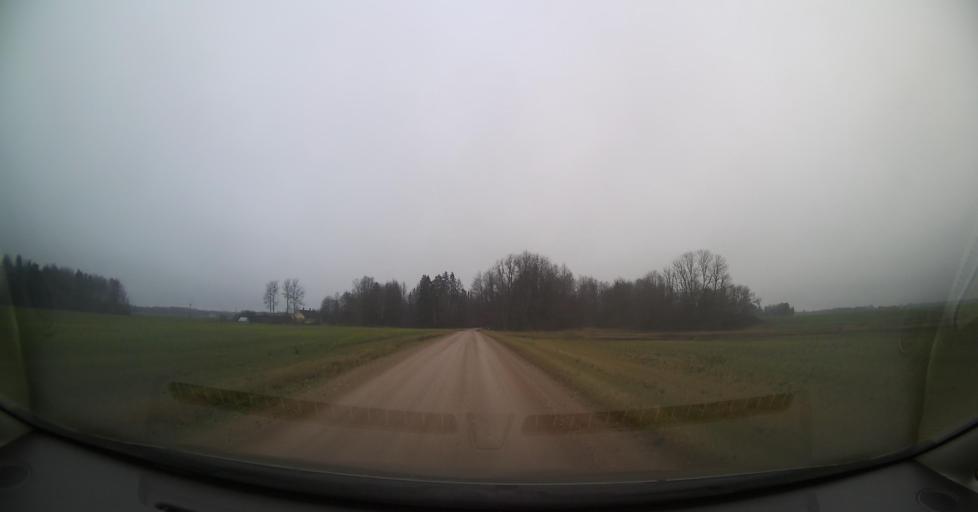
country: EE
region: Tartu
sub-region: Tartu linn
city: Tartu
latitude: 58.3767
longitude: 26.9285
